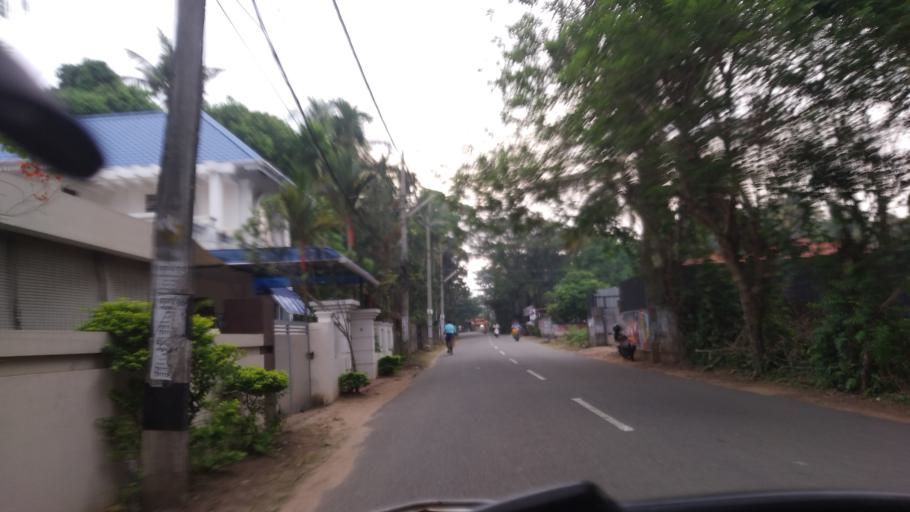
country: IN
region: Kerala
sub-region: Ernakulam
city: Elur
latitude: 10.1339
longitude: 76.2446
